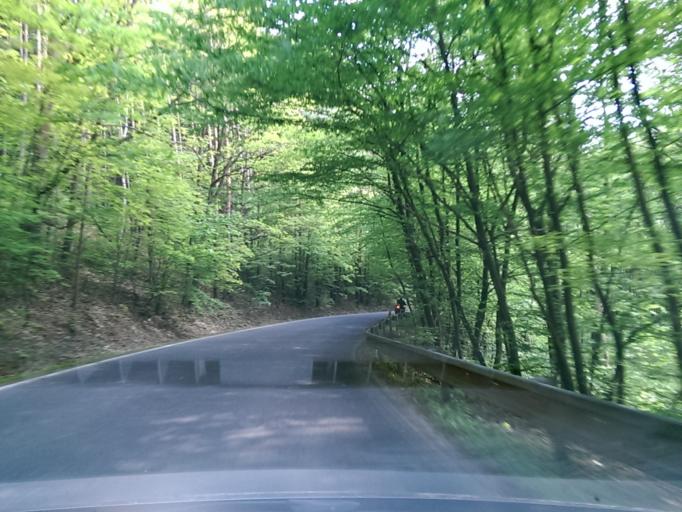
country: CZ
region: Central Bohemia
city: Bela pod Bezdezem
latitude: 50.4967
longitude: 14.8577
